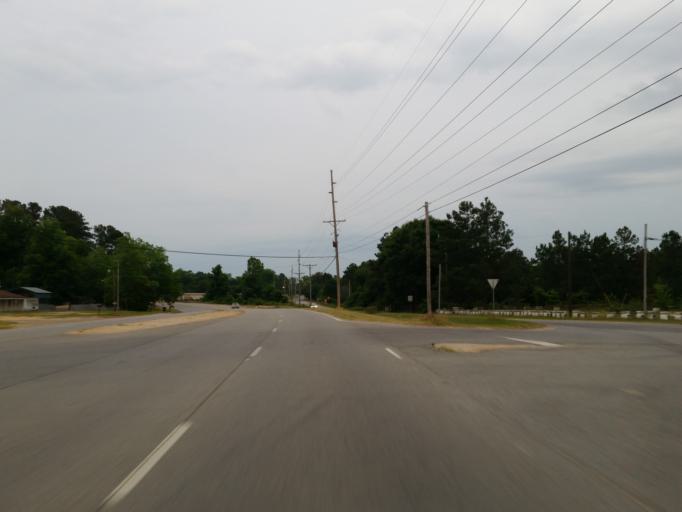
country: US
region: Georgia
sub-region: Crisp County
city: Cordele
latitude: 31.9867
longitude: -83.7927
